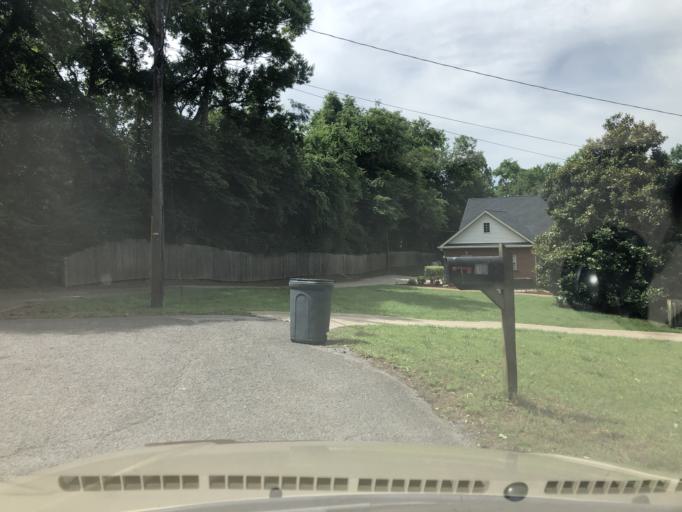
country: US
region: Tennessee
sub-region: Davidson County
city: Lakewood
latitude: 36.2567
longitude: -86.6218
